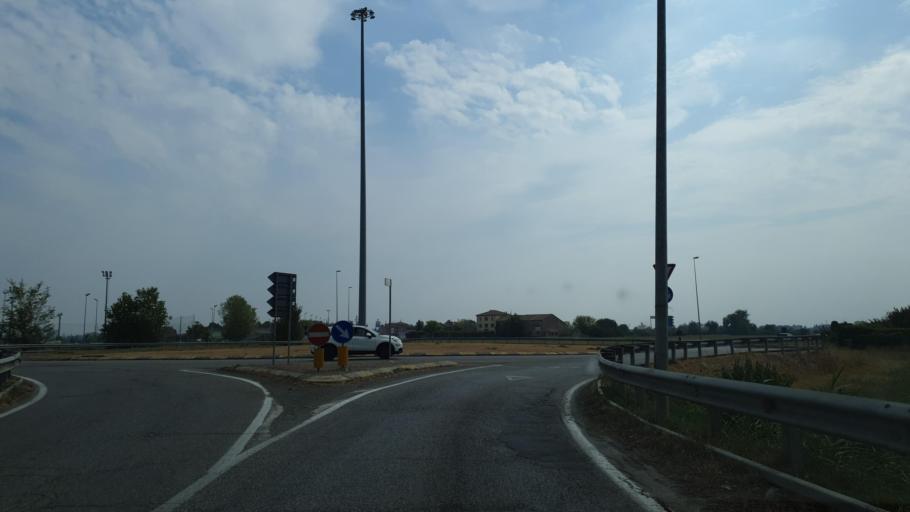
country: IT
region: Emilia-Romagna
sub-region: Provincia di Parma
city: Baganzola
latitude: 44.8304
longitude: 10.2745
